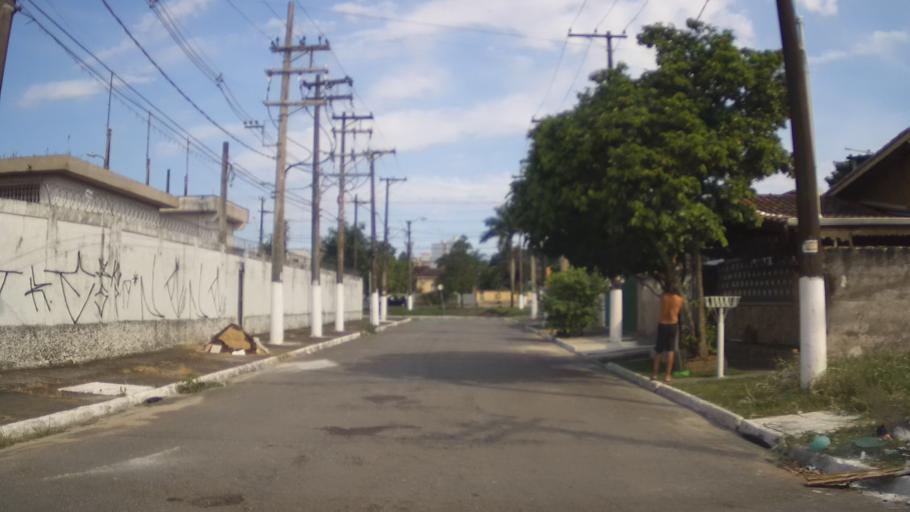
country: BR
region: Sao Paulo
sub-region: Praia Grande
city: Praia Grande
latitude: -24.0009
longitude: -46.4275
